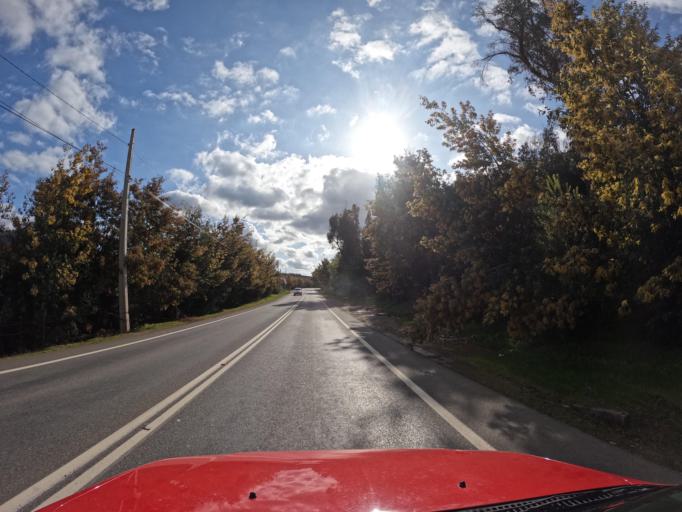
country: CL
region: Maule
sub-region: Provincia de Talca
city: Constitucion
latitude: -35.5371
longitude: -72.1625
